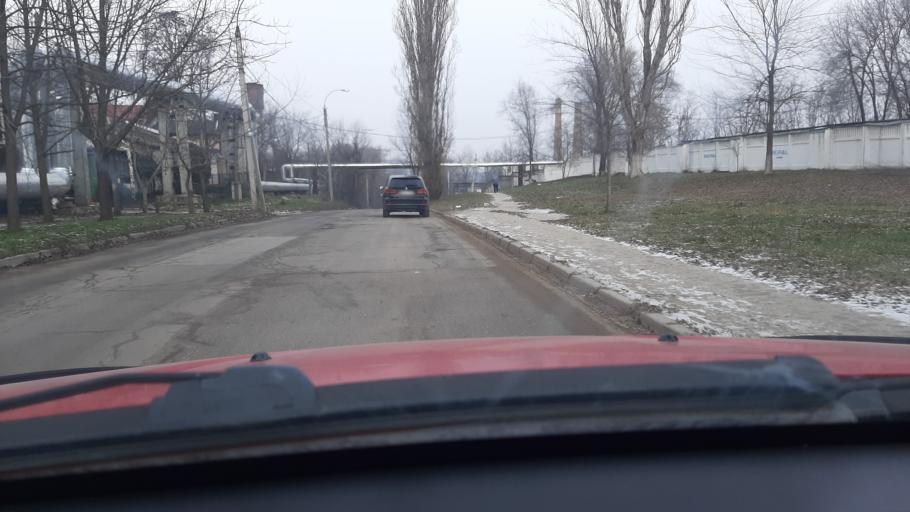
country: MD
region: Chisinau
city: Chisinau
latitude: 46.9769
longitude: 28.8926
